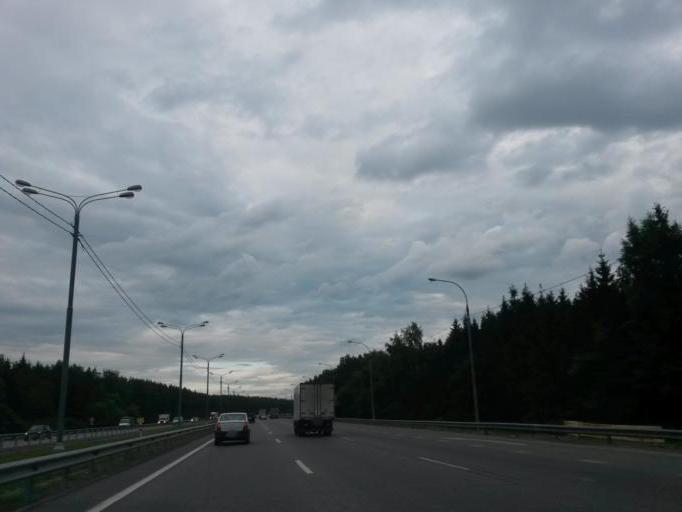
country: RU
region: Moskovskaya
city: Domodedovo
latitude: 55.4533
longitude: 37.7839
